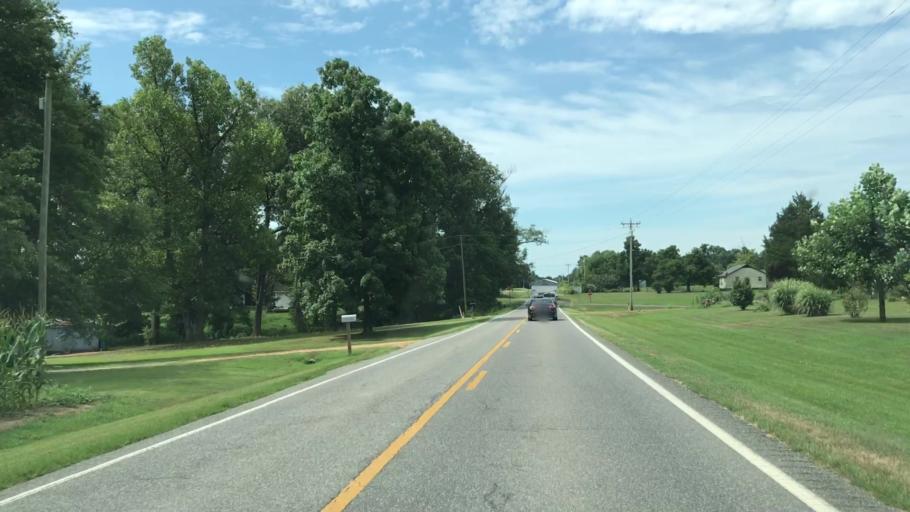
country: US
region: Kentucky
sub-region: Graves County
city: Mayfield
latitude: 36.8479
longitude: -88.5752
